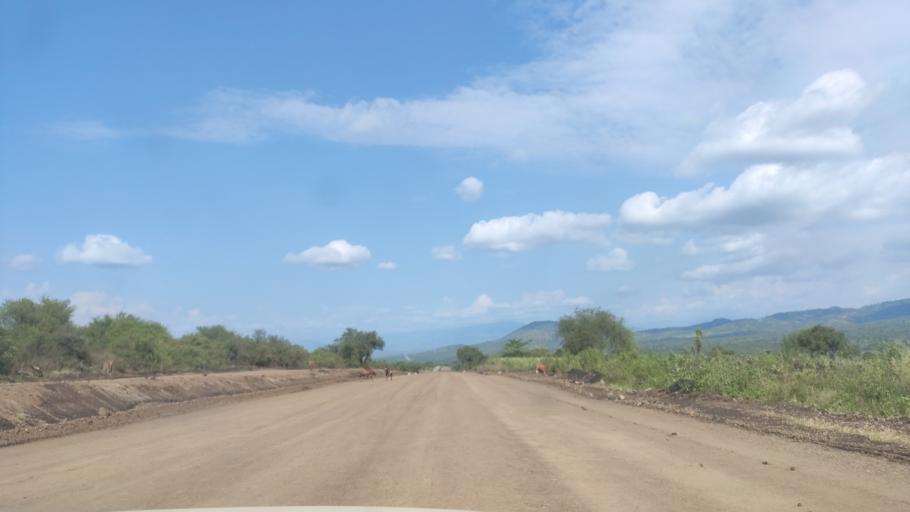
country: ET
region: Southern Nations, Nationalities, and People's Region
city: Felege Neway
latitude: 6.3983
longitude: 37.1158
